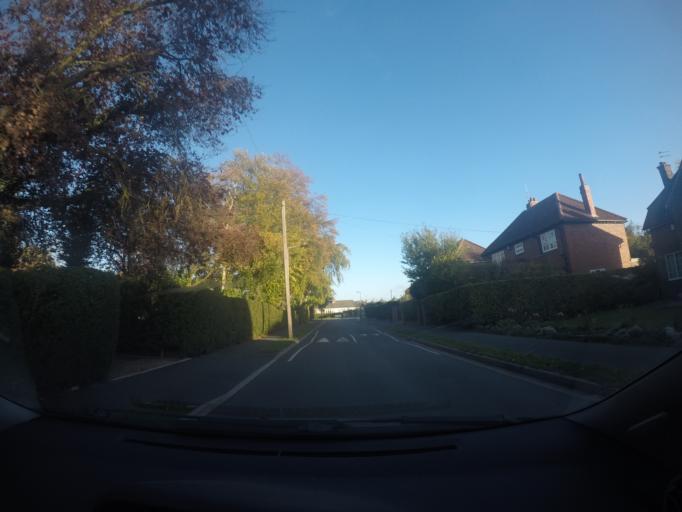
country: GB
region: England
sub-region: City of York
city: Huntington
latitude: 53.9853
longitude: -1.0679
